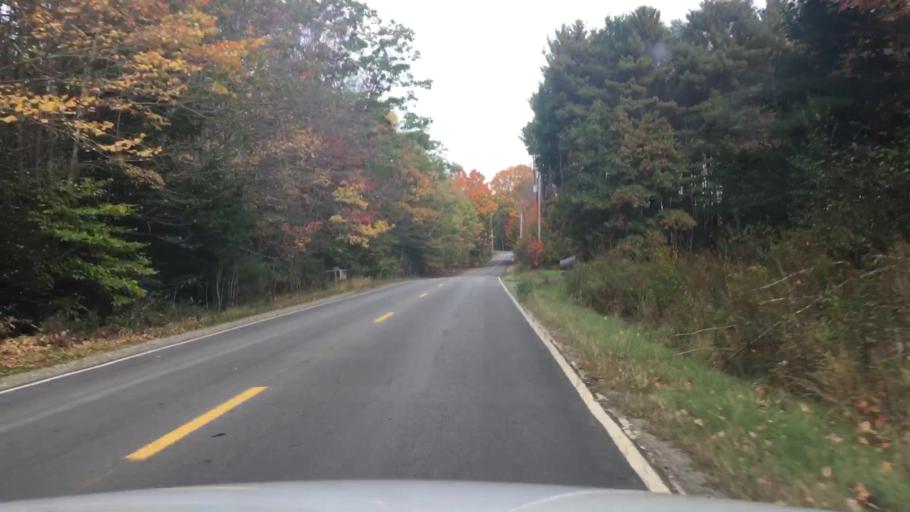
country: US
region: Maine
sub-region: Waldo County
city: Searsmont
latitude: 44.4175
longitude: -69.1400
